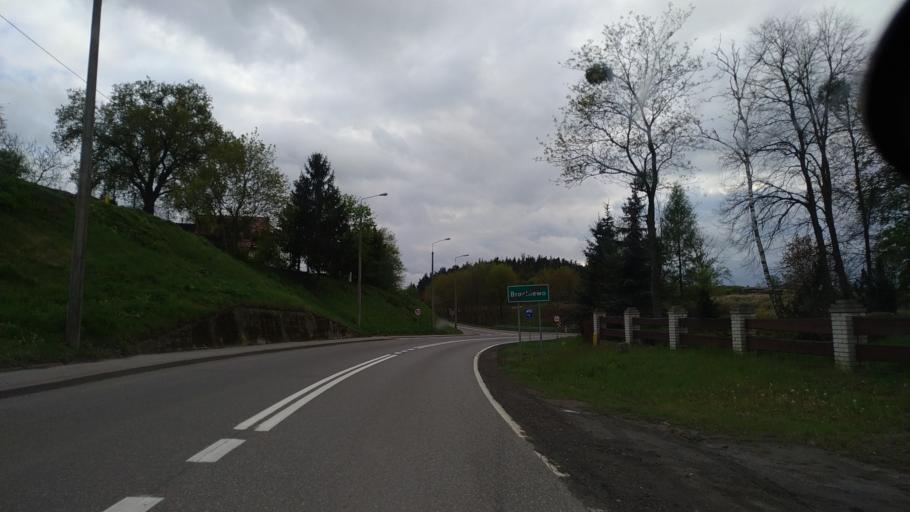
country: PL
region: Pomeranian Voivodeship
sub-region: Powiat kwidzynski
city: Ryjewo
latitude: 53.7987
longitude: 18.9646
